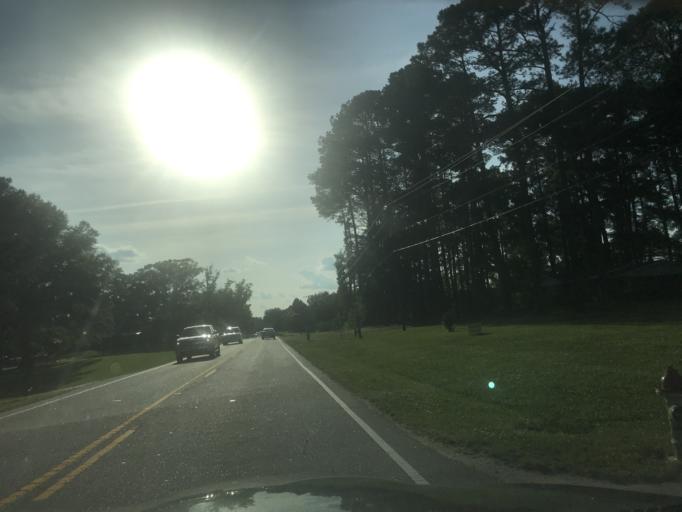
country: US
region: North Carolina
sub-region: Wake County
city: Knightdale
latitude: 35.7527
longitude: -78.4985
